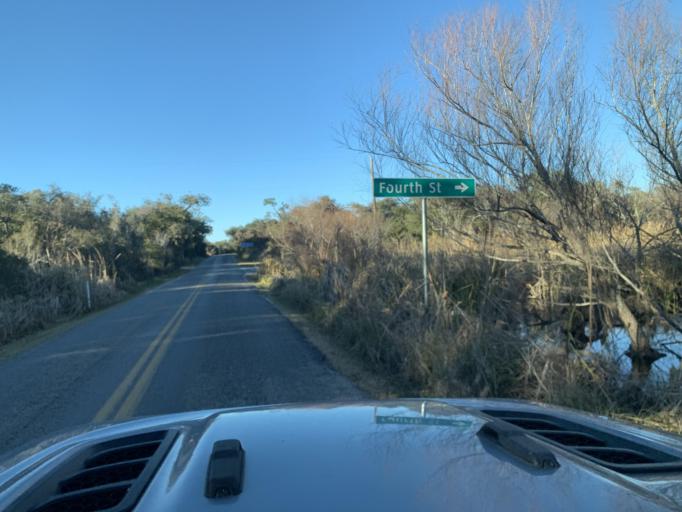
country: US
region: Texas
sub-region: Aransas County
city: Fulton
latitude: 28.1424
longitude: -96.9843
